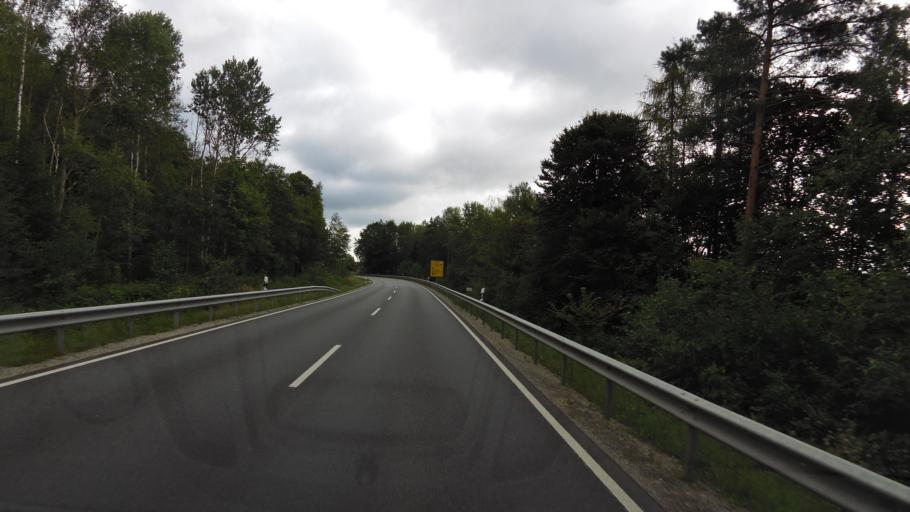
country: DE
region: Bavaria
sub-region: Lower Bavaria
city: Loitzendorf
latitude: 49.1037
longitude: 12.6497
